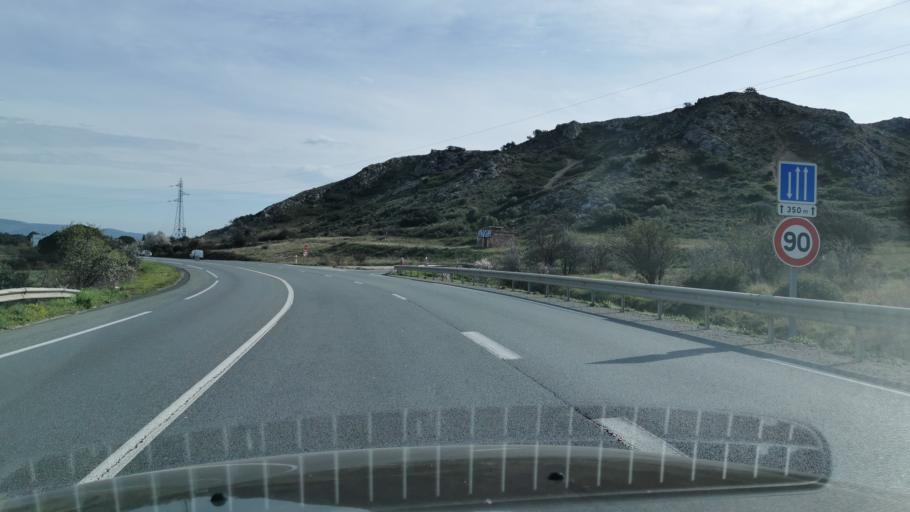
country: FR
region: Languedoc-Roussillon
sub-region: Departement de l'Aude
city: Narbonne
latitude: 43.1786
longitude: 2.9684
